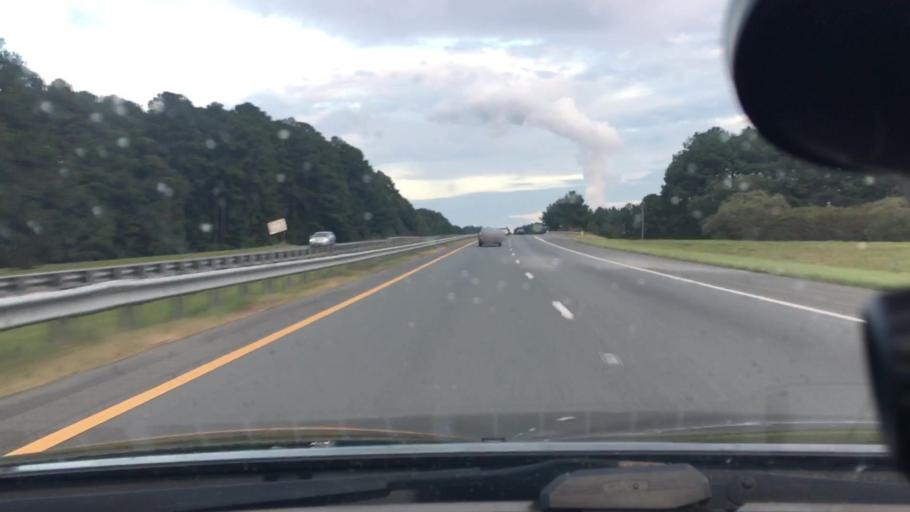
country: US
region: North Carolina
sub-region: Wake County
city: Green Level
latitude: 35.6444
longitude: -79.0061
